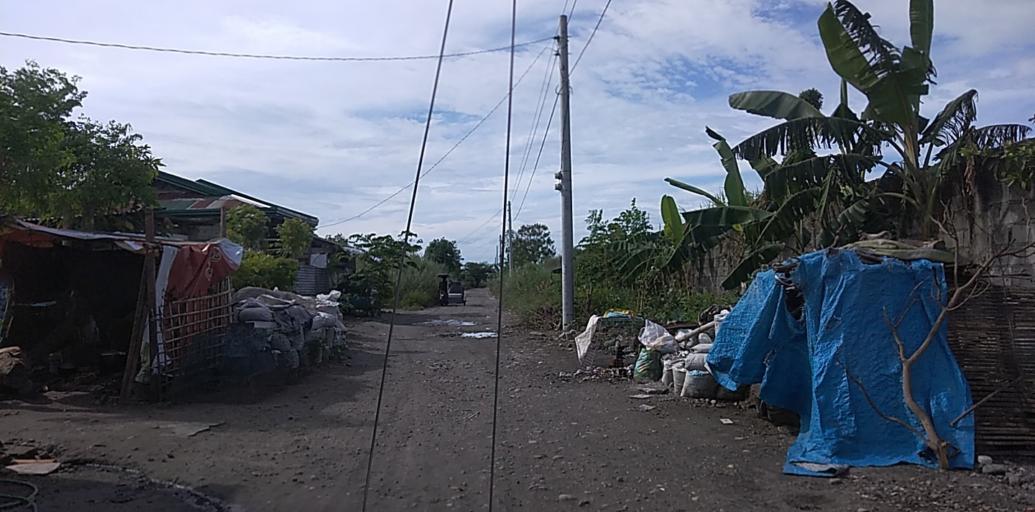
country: PH
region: Central Luzon
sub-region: Province of Pampanga
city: Angeles City
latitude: 15.1296
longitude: 120.5557
